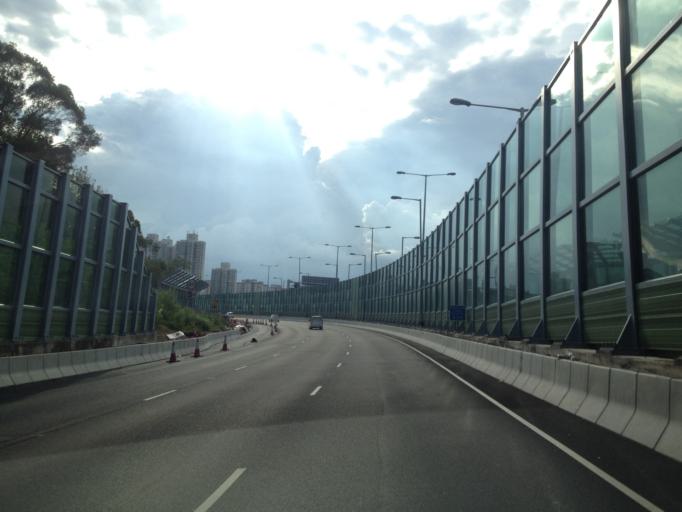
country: HK
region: Tai Po
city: Tai Po
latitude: 22.4449
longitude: 114.1766
